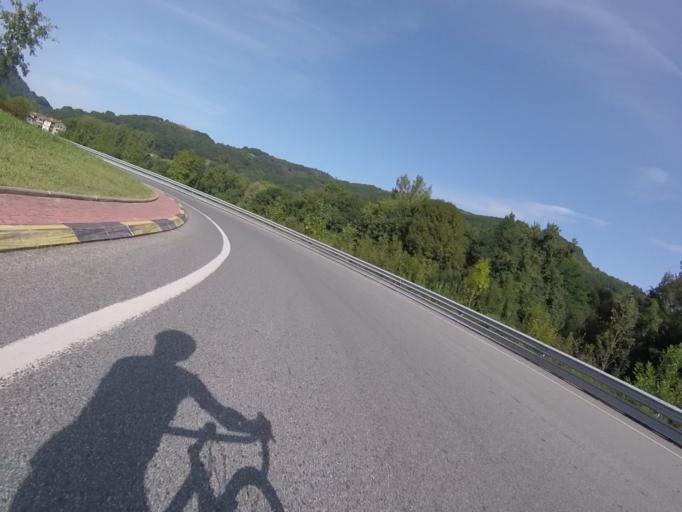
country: ES
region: Navarre
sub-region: Provincia de Navarra
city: Doneztebe
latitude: 43.1413
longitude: -1.5622
